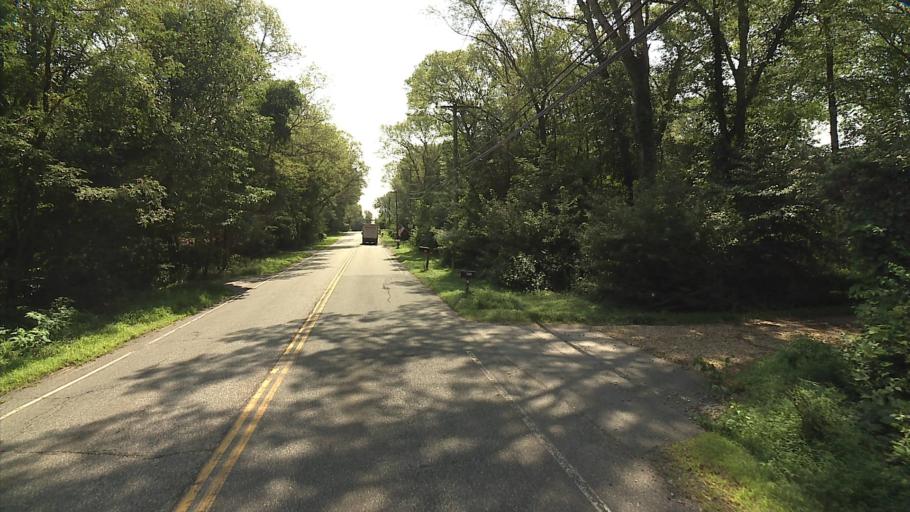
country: US
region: Connecticut
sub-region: New London County
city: Montville Center
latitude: 41.5002
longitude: -72.2308
